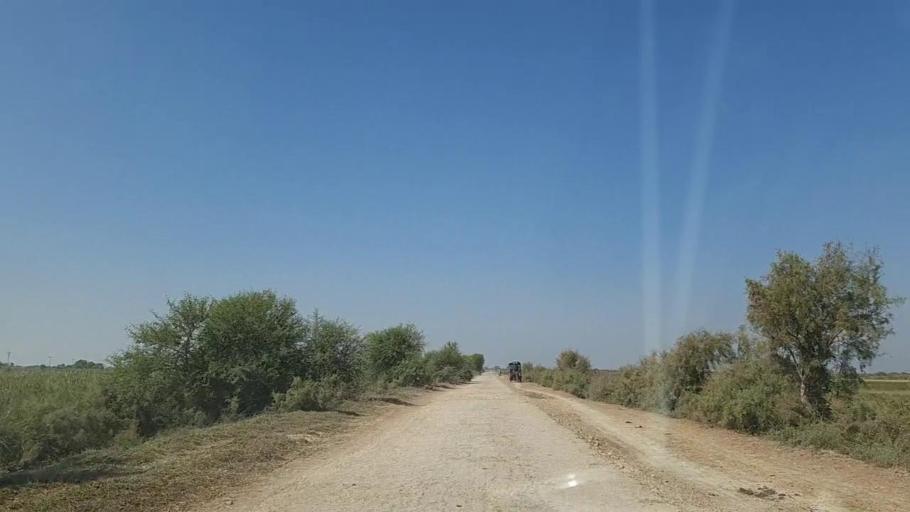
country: PK
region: Sindh
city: Chuhar Jamali
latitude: 24.4209
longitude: 68.0138
